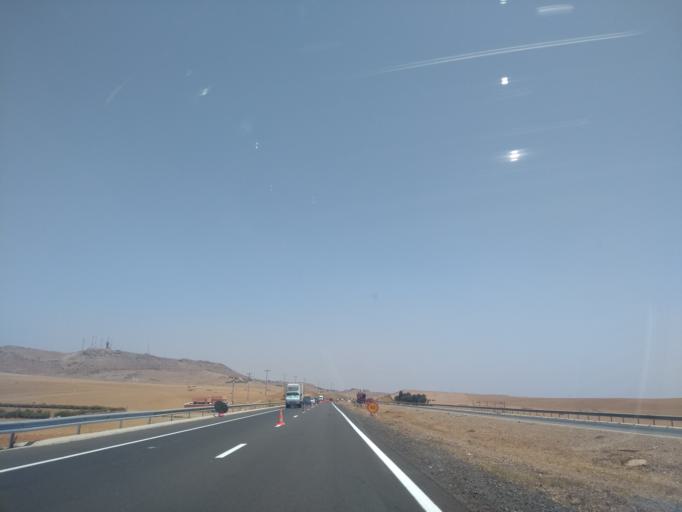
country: MA
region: Marrakech-Tensift-Al Haouz
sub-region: Kelaa-Des-Sraghna
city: Sidi Abdallah
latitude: 32.4540
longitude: -7.9312
